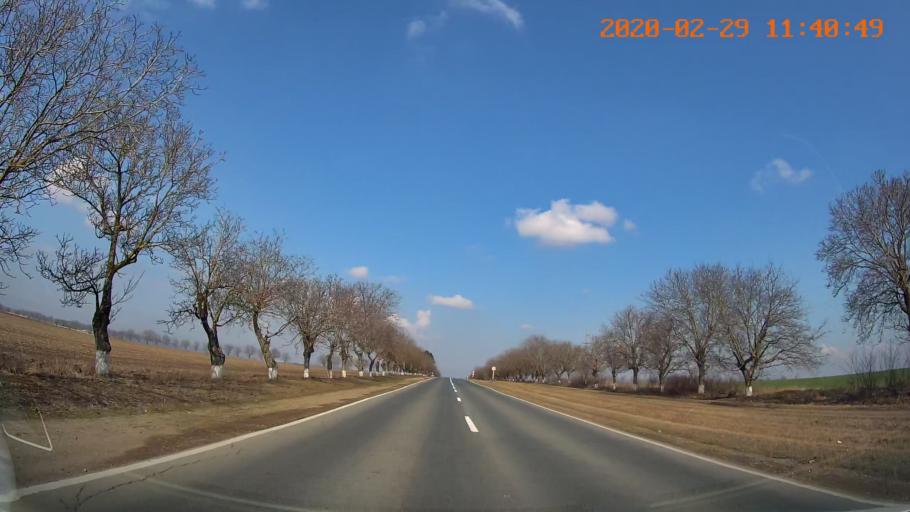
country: MD
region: Rezina
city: Saharna
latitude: 47.6622
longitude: 29.0187
